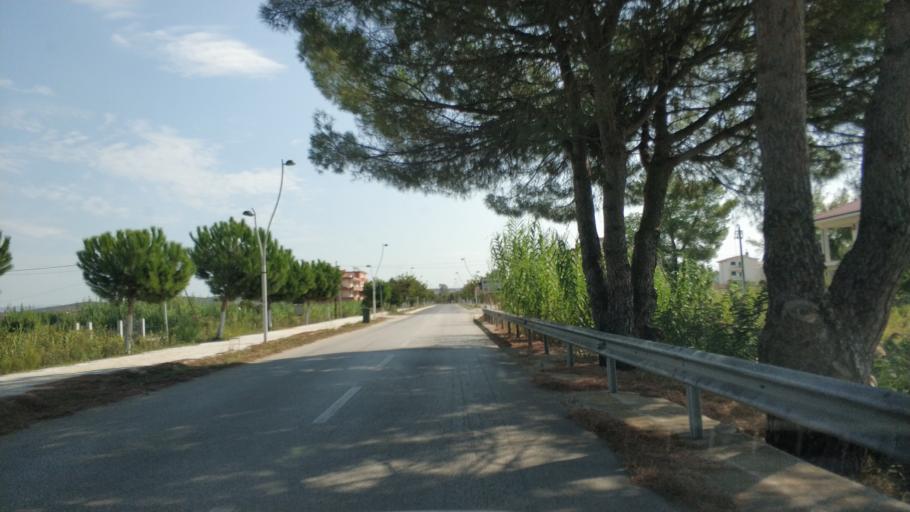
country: AL
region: Fier
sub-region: Rrethi i Lushnjes
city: Divjake
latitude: 40.9923
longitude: 19.5172
